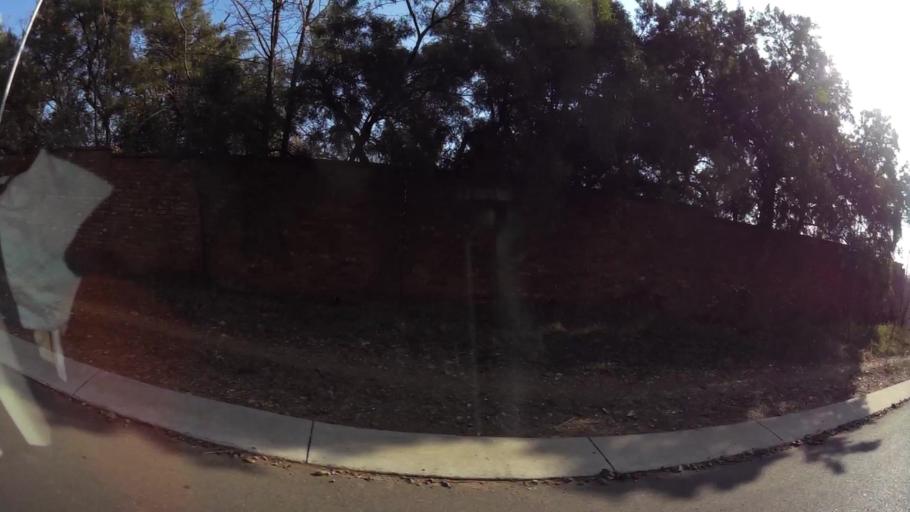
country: ZA
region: Gauteng
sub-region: City of Tshwane Metropolitan Municipality
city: Pretoria
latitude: -25.7576
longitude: 28.3287
